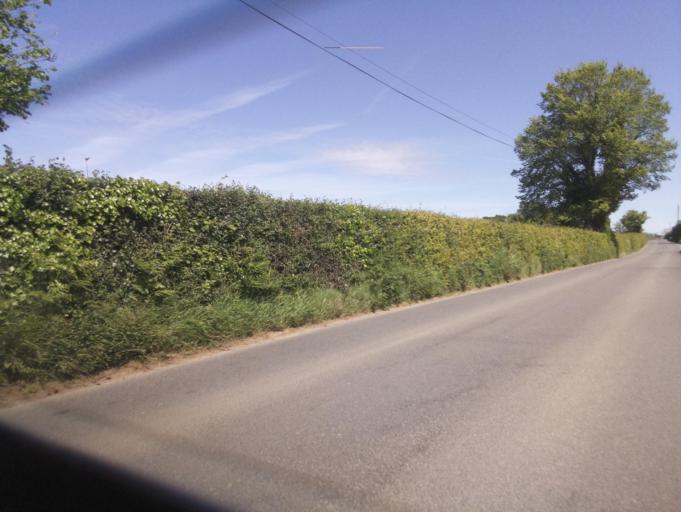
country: GB
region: England
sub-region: Devon
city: Ottery St Mary
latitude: 50.7611
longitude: -3.2710
